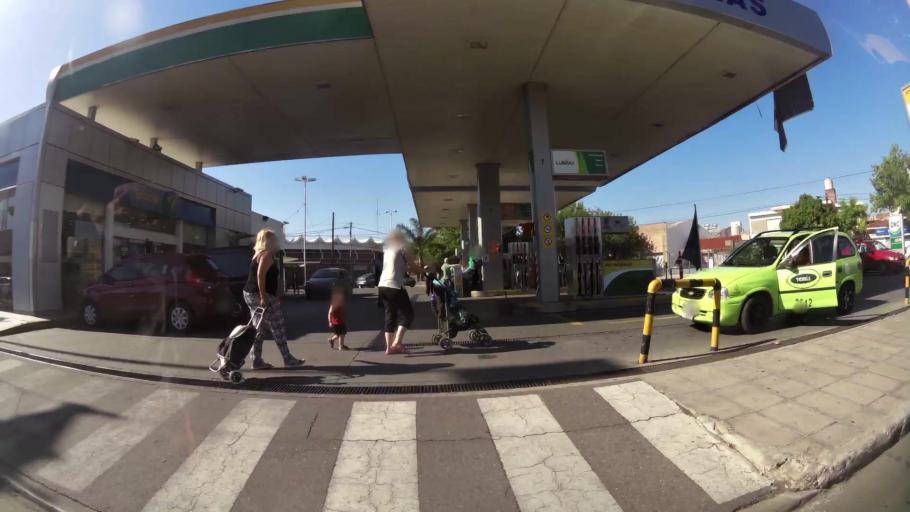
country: AR
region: Cordoba
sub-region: Departamento de Capital
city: Cordoba
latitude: -31.4333
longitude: -64.1589
